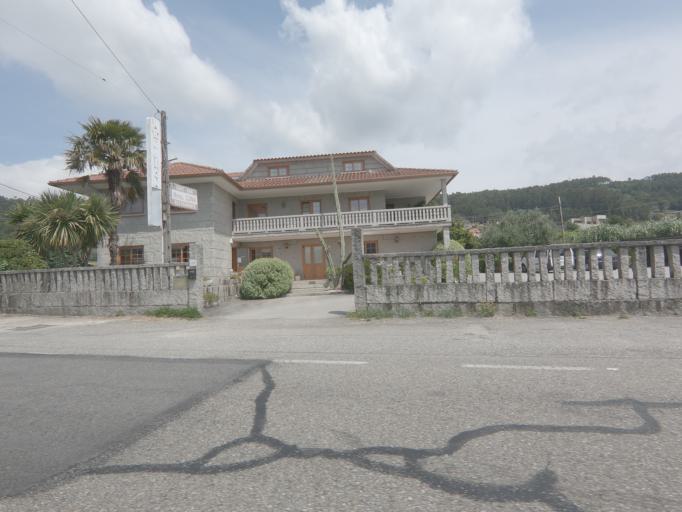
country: ES
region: Galicia
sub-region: Provincia de Pontevedra
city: Tomino
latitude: 42.0353
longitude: -8.7289
